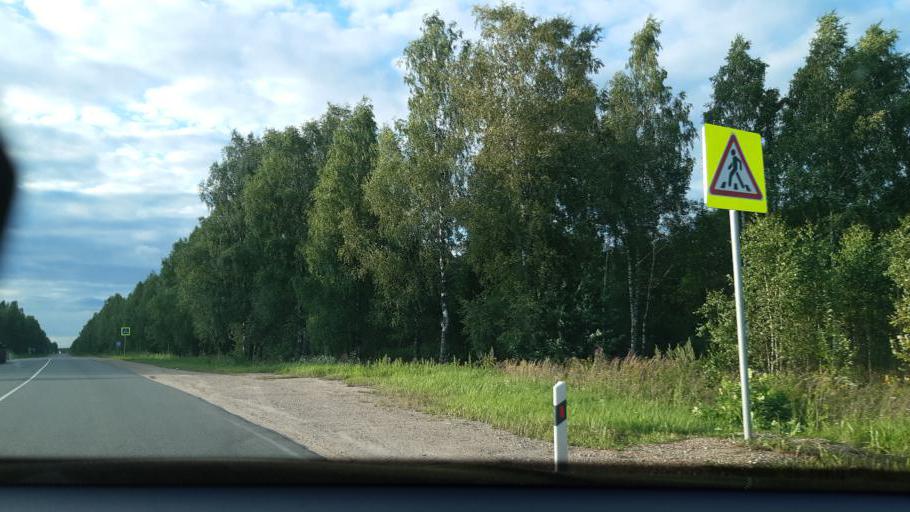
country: RU
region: Smolensk
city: Yel'nya
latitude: 54.5949
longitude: 33.1895
